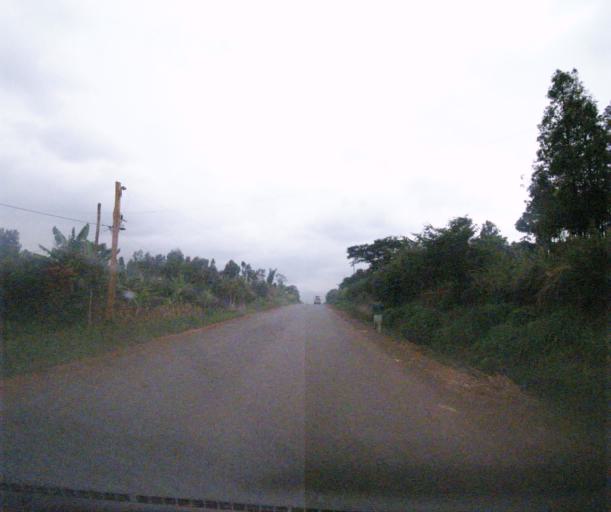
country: CM
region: West
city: Bansoa
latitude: 5.4905
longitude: 10.1905
